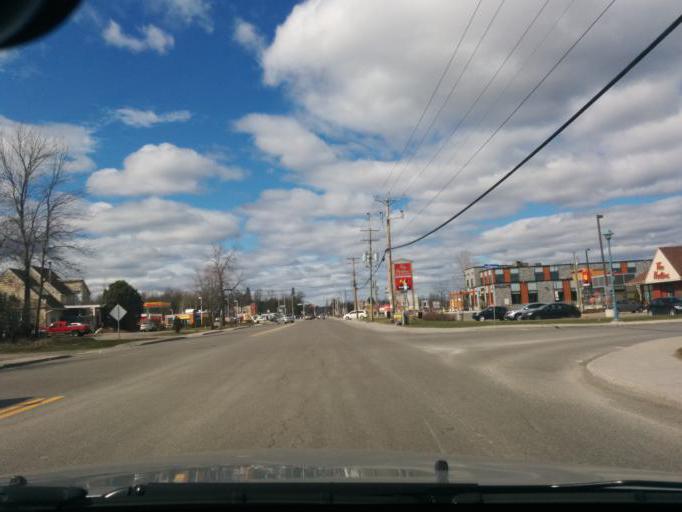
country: CA
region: Ontario
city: Bells Corners
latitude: 45.4132
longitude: -75.8084
